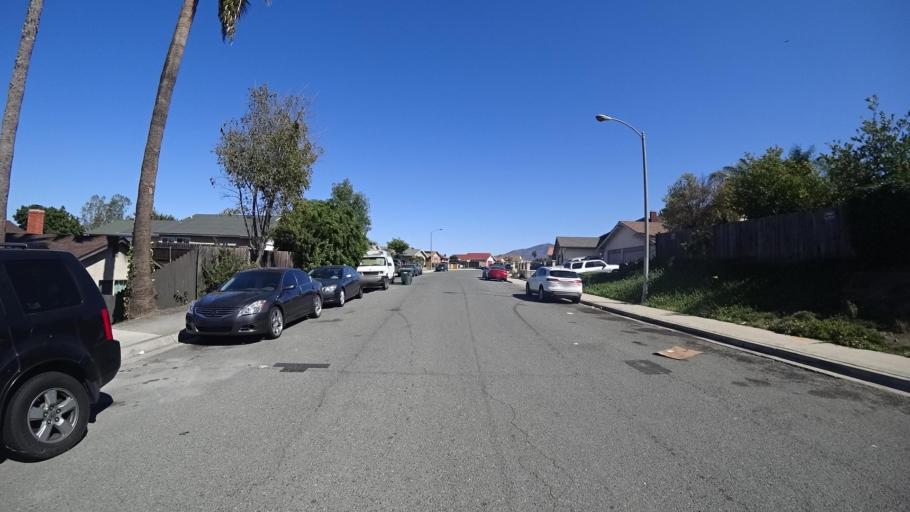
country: US
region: California
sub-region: San Diego County
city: La Presa
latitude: 32.6988
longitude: -117.0230
